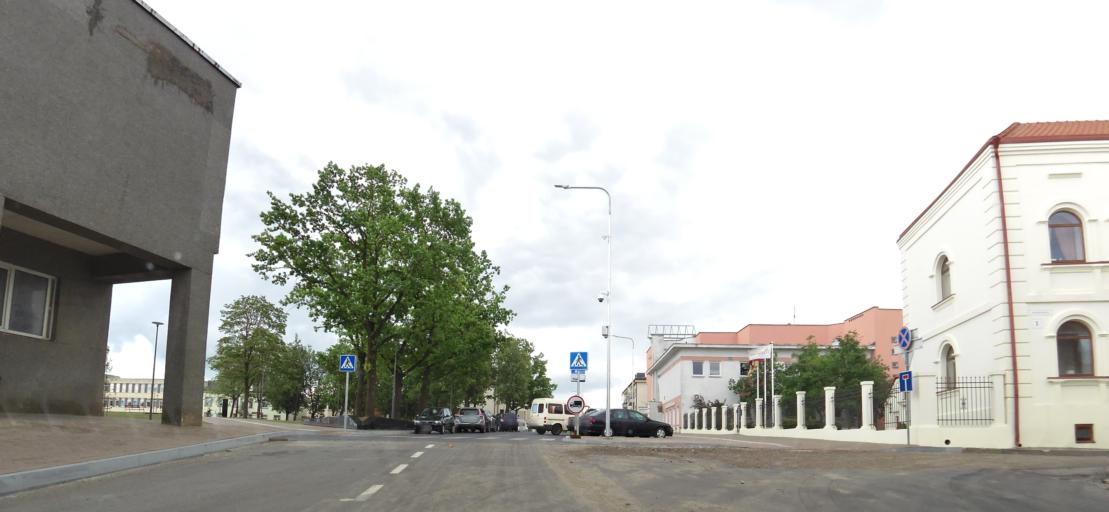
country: LT
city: Kupiskis
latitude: 55.8391
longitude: 24.9737
